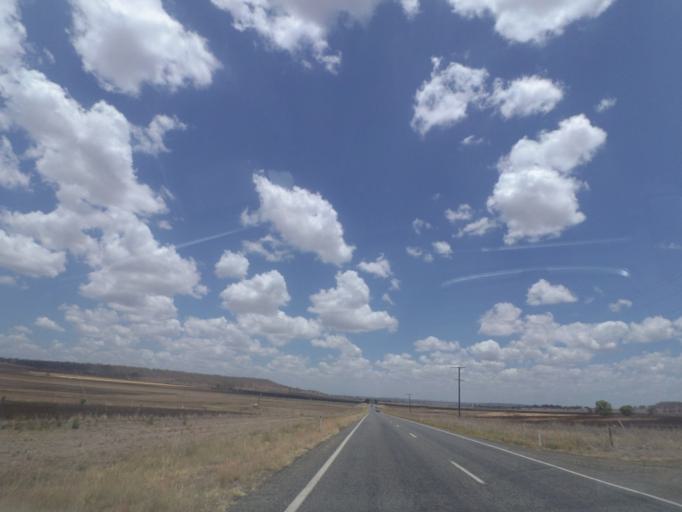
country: AU
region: Queensland
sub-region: Southern Downs
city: Warwick
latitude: -28.0004
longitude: 151.9935
